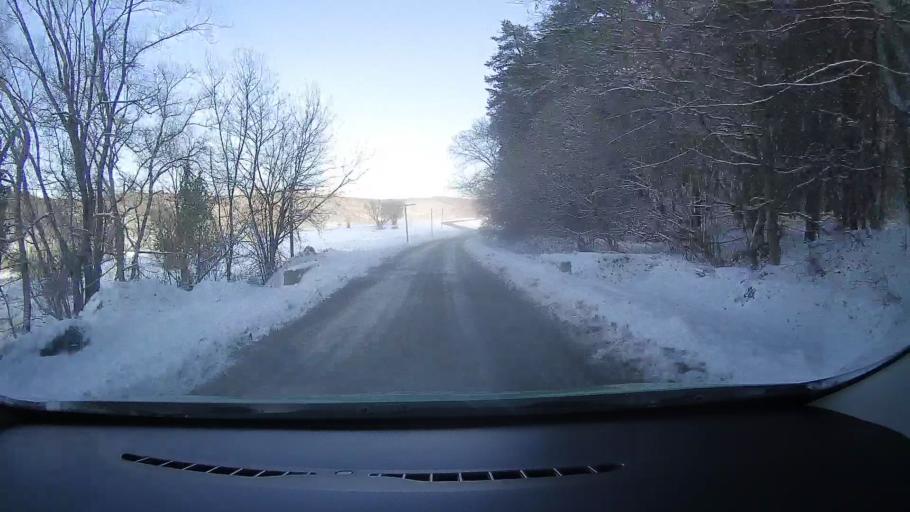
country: RO
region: Sibiu
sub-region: Comuna Mosna
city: Mosna
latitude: 46.0189
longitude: 24.4124
